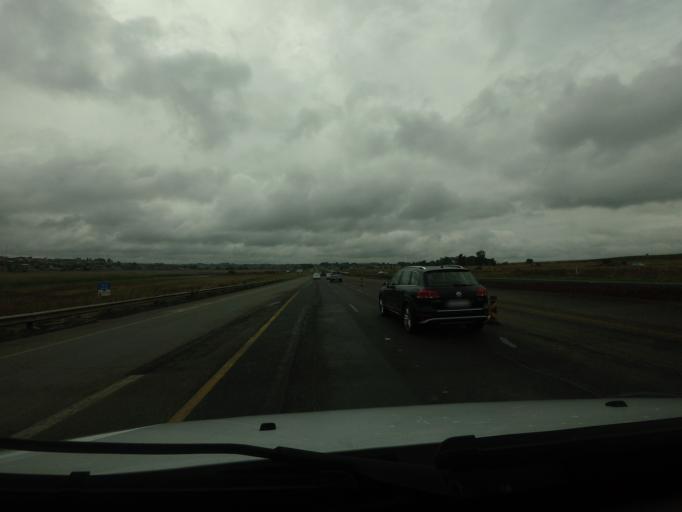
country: ZA
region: Mpumalanga
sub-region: Nkangala District Municipality
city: Witbank
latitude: -25.8802
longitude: 29.1677
